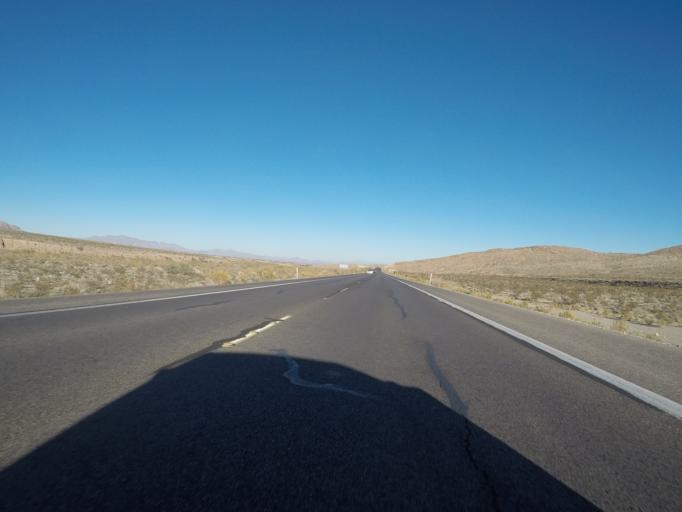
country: US
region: Nevada
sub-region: Clark County
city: Summerlin South
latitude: 36.1459
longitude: -115.3843
